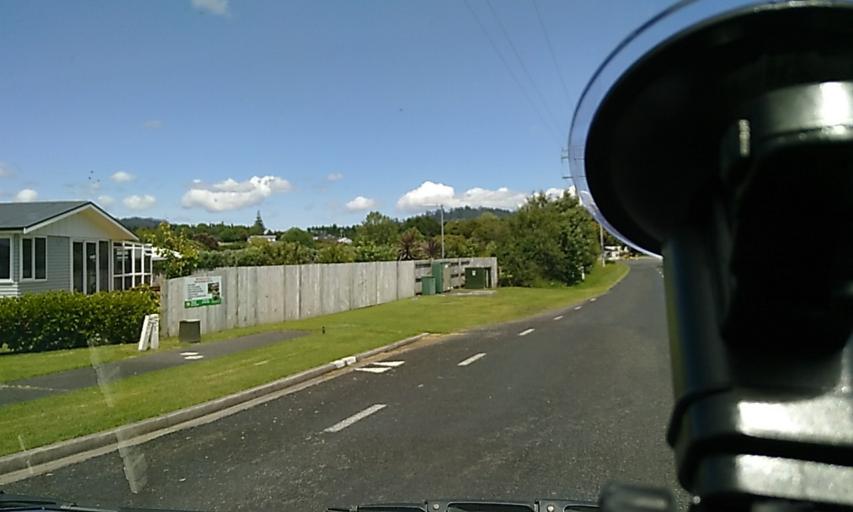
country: NZ
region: Bay of Plenty
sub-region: Western Bay of Plenty District
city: Waihi Beach
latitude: -37.4465
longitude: 175.9598
